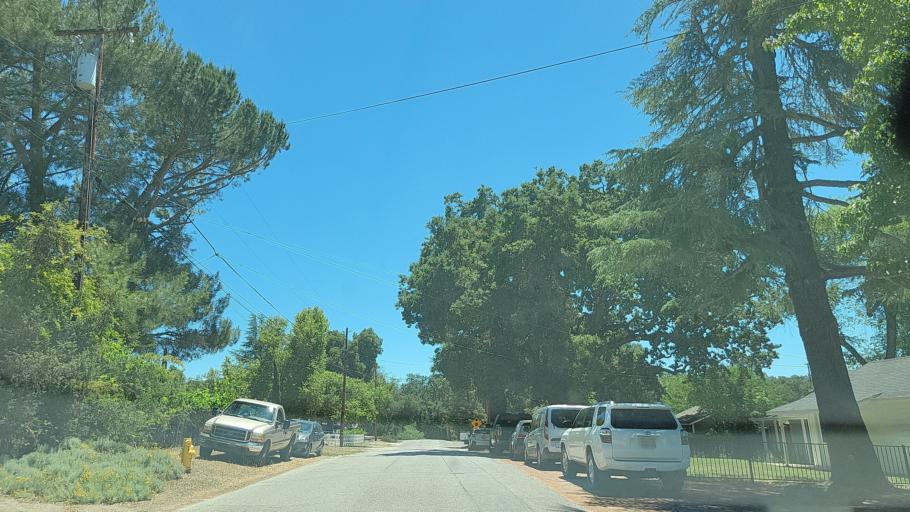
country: US
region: California
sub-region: San Luis Obispo County
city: Atascadero
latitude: 35.4735
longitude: -120.6635
